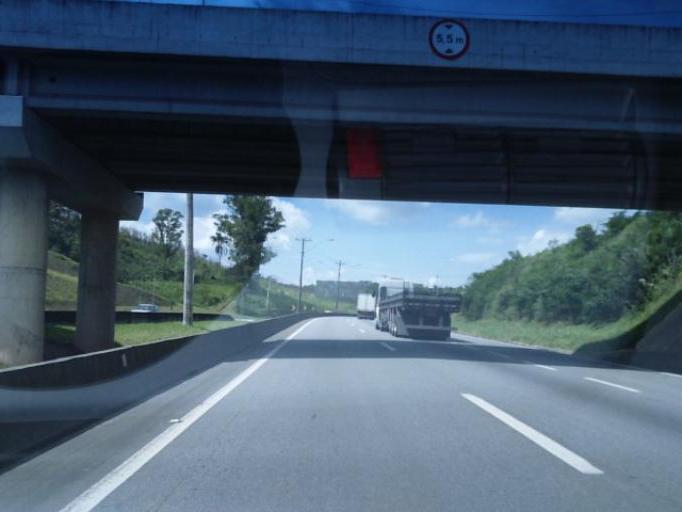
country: BR
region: Sao Paulo
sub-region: Sao Lourenco Da Serra
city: Sao Lourenco da Serra
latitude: -23.8016
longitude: -46.9173
